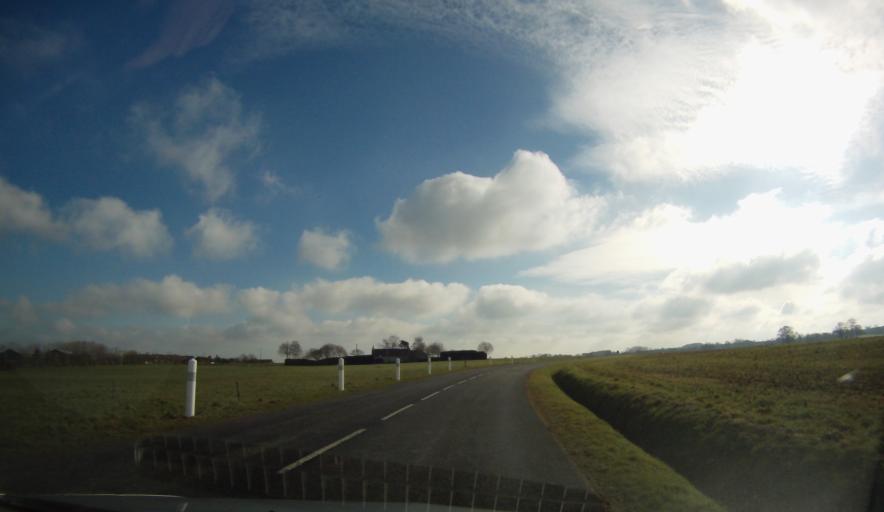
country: FR
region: Brittany
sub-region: Departement d'Ille-et-Vilaine
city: Corps-Nuds
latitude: 47.9477
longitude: -1.5655
